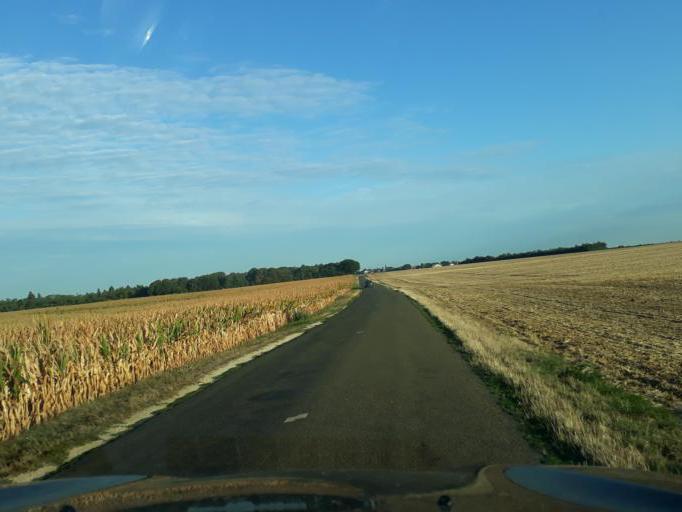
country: FR
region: Centre
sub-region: Departement du Loir-et-Cher
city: Ouzouer-le-Marche
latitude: 47.9549
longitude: 1.5570
